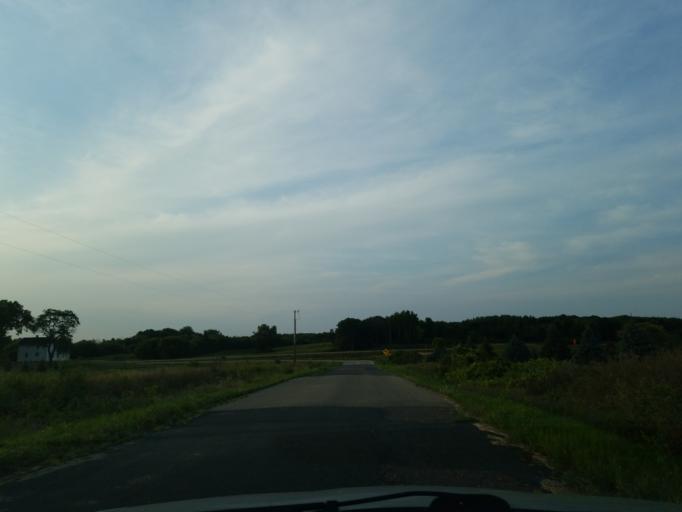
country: US
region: Minnesota
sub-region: Washington County
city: Stillwater
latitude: 45.0698
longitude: -92.7609
